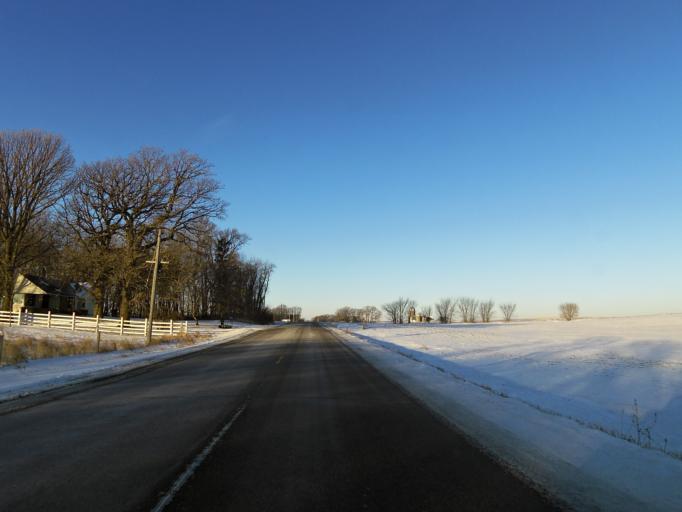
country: US
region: Minnesota
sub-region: Scott County
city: Prior Lake
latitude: 44.6525
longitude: -93.4859
